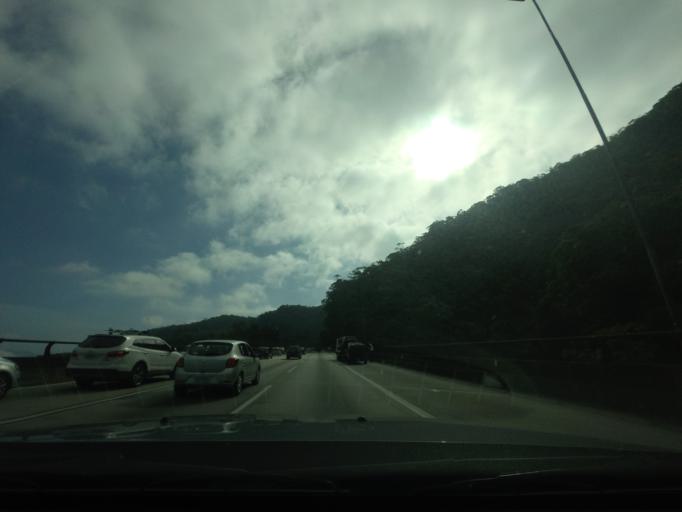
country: BR
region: Sao Paulo
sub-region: Cubatao
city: Cubatao
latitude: -23.9177
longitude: -46.5263
